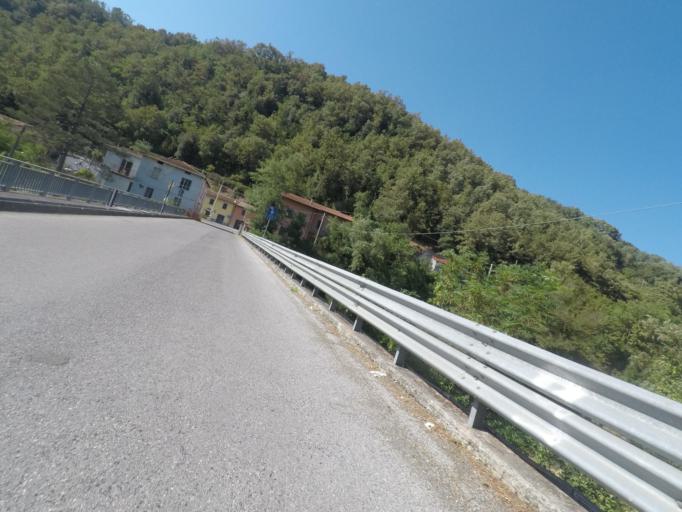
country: IT
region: Tuscany
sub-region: Provincia di Massa-Carrara
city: Pallerone
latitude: 44.2023
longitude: 10.0624
